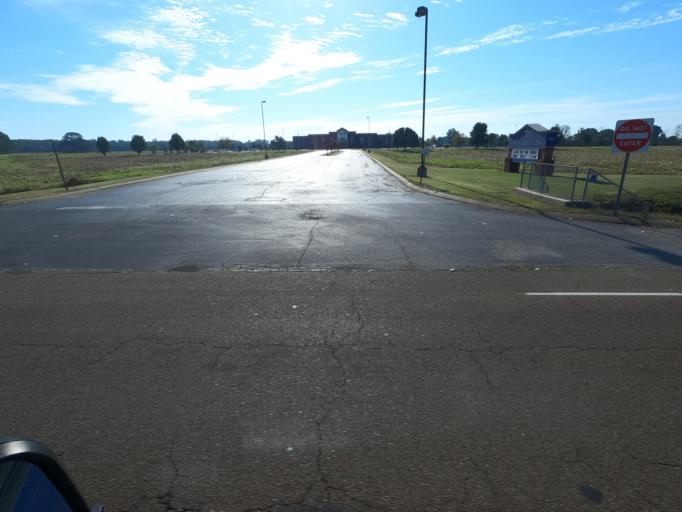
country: US
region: Tennessee
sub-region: Shelby County
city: Millington
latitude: 35.3699
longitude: -89.8832
